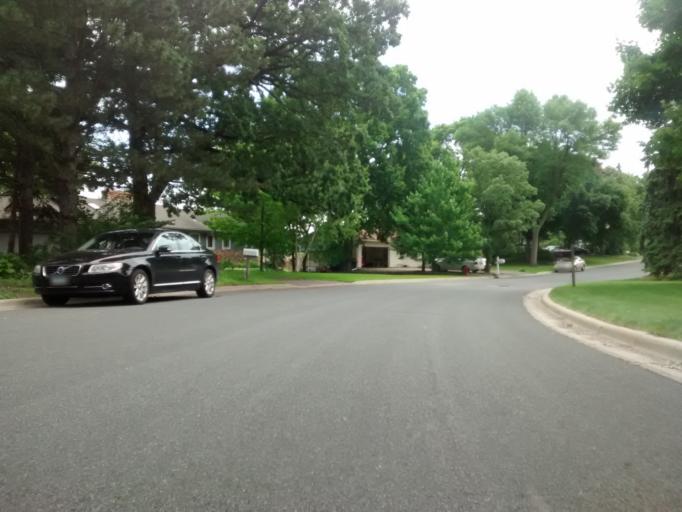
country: US
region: Minnesota
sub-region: Dakota County
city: Burnsville
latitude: 44.7550
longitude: -93.2889
